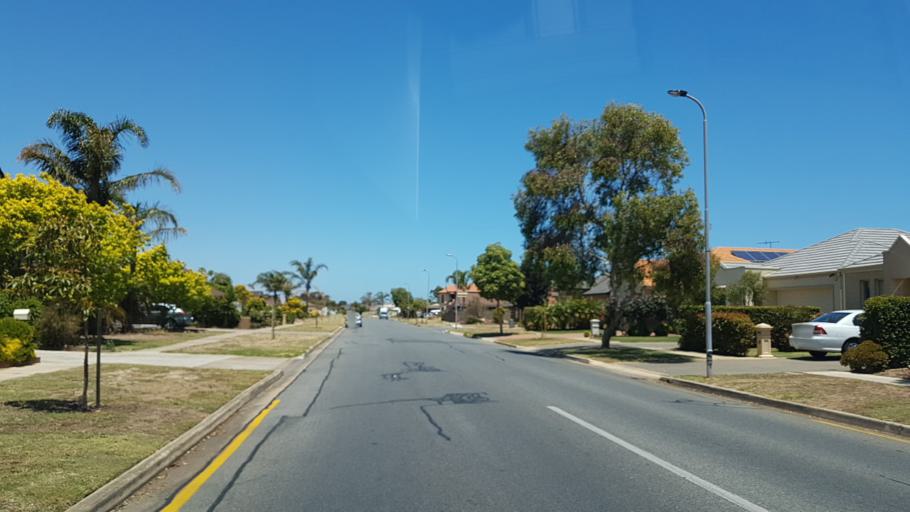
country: AU
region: South Australia
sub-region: Charles Sturt
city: West Lakes Shore
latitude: -34.8571
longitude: 138.4881
